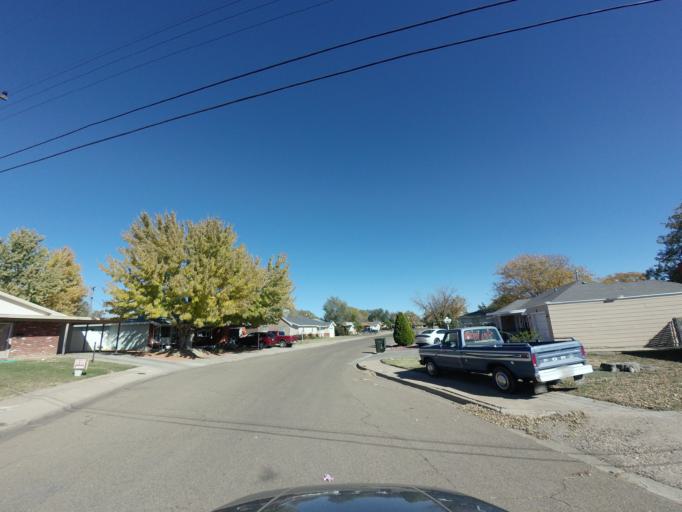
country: US
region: New Mexico
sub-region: Curry County
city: Clovis
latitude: 34.4206
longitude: -103.2048
